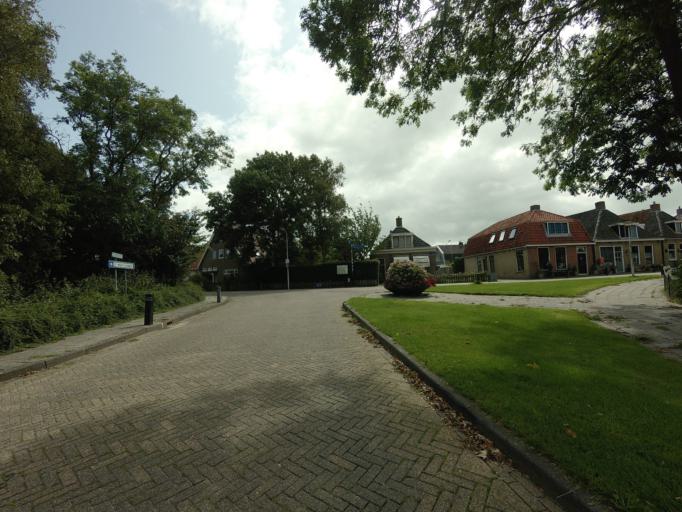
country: NL
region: Friesland
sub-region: Sudwest Fryslan
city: Makkum
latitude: 53.0846
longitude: 5.4242
